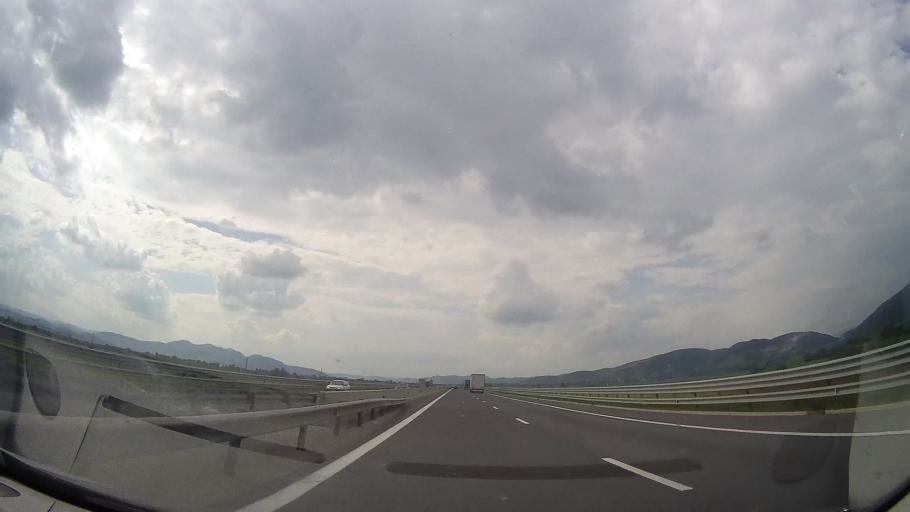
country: RO
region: Hunedoara
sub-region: Oras Simeria
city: Simeria
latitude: 45.8706
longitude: 23.0163
